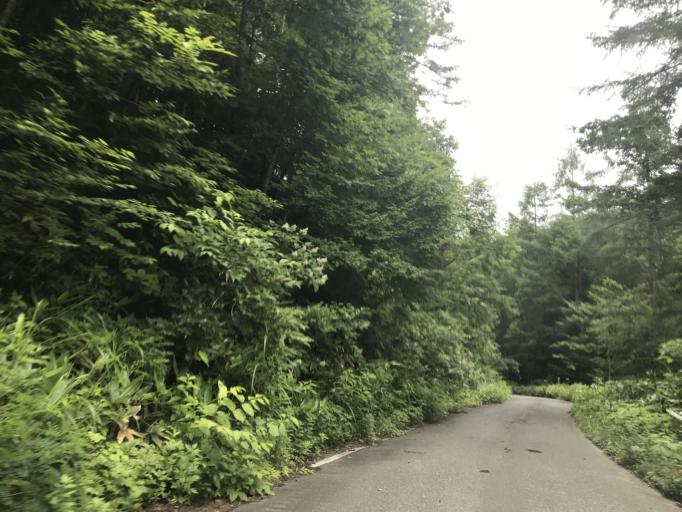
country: JP
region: Iwate
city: Ichinoseki
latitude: 38.9466
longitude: 140.8768
